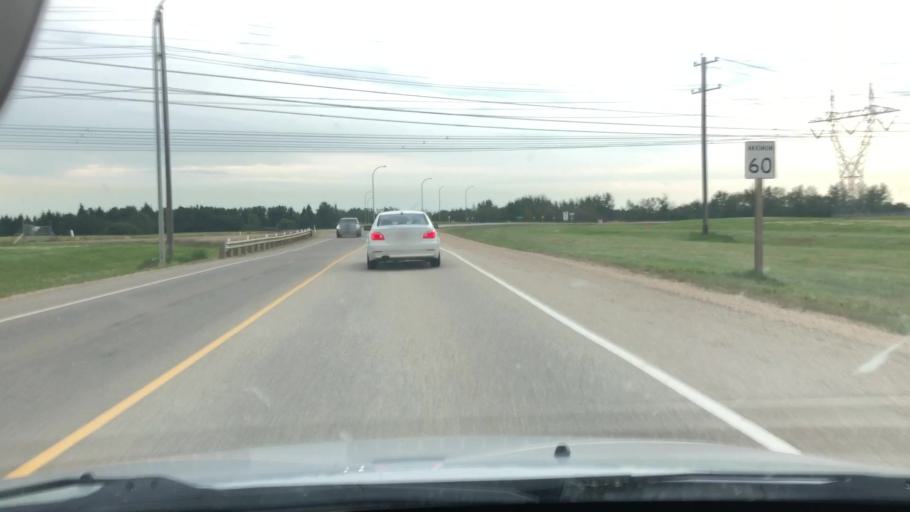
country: CA
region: Alberta
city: Devon
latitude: 53.4624
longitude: -113.6364
